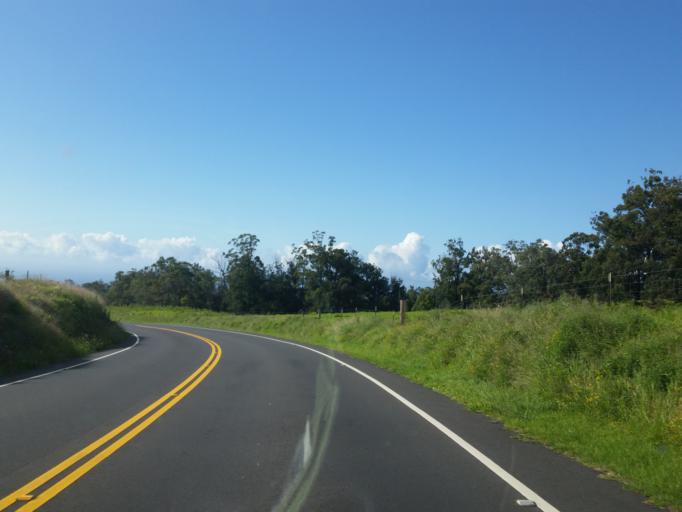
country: US
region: Hawaii
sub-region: Maui County
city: Pukalani
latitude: 20.8173
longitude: -156.3056
